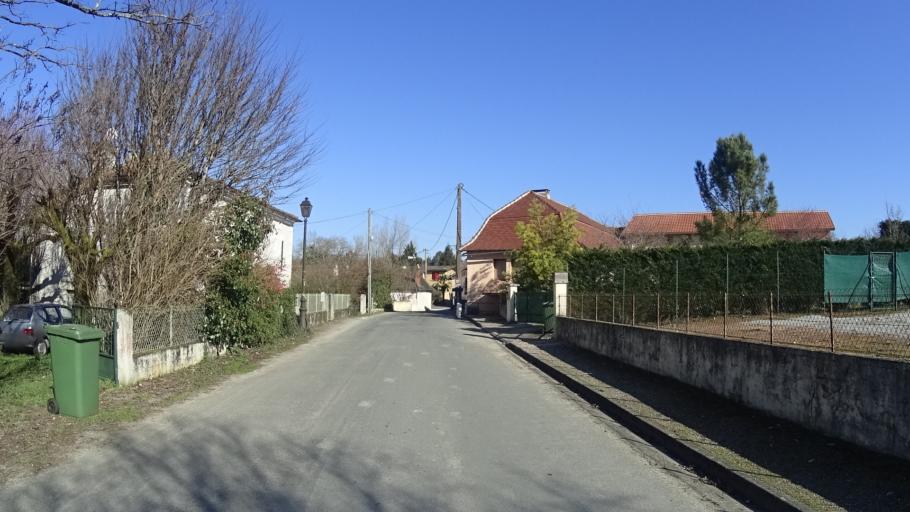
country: FR
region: Aquitaine
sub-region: Departement de la Dordogne
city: Montpon-Menesterol
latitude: 45.0374
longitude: 0.2538
